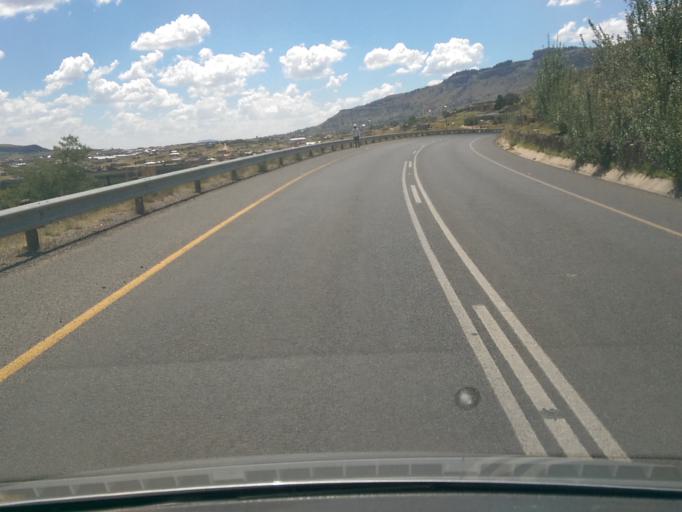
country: LS
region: Maseru
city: Maseru
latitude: -29.3793
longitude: 27.4965
